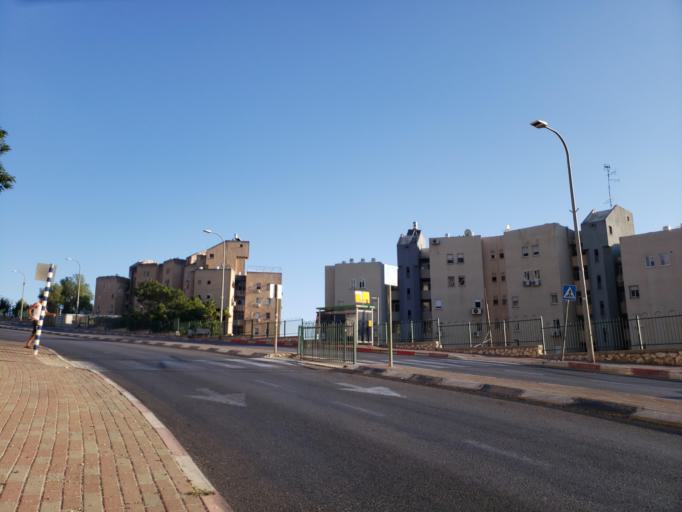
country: IL
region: Northern District
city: Safed
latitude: 32.9596
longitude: 35.4903
